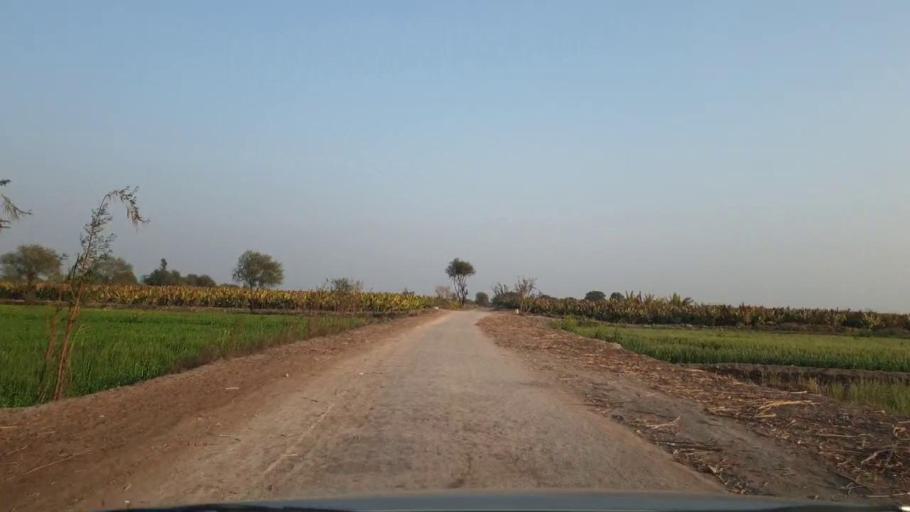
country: PK
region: Sindh
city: Tando Adam
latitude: 25.7120
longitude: 68.5991
